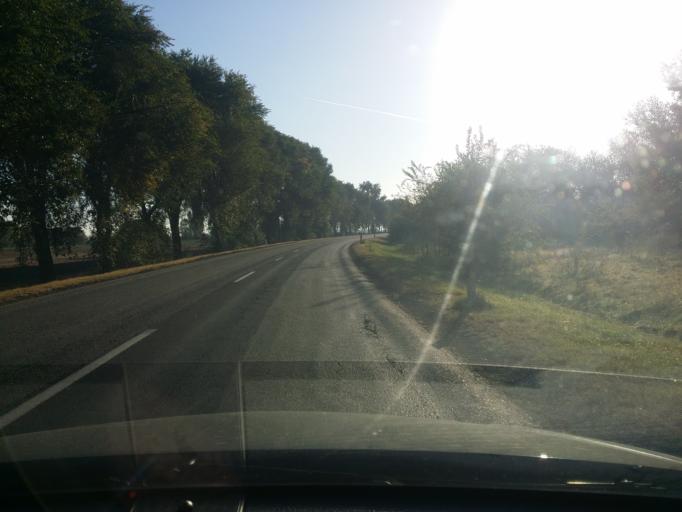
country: HU
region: Bacs-Kiskun
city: Nyarlorinc
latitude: 46.9155
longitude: 19.7962
